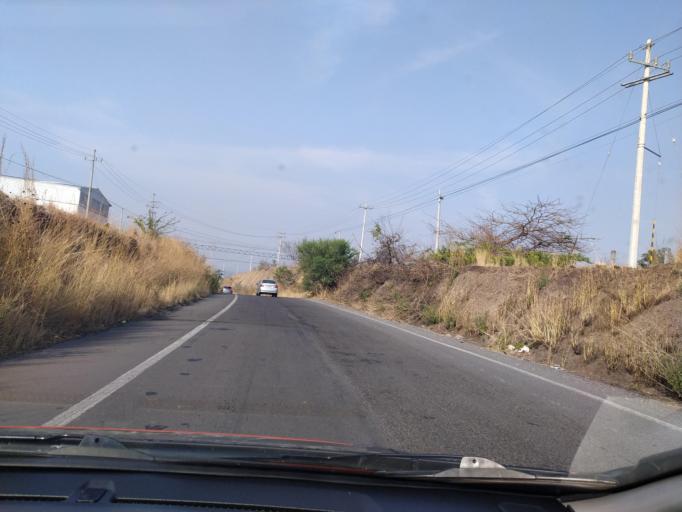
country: MX
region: Jalisco
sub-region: Acatlan de Juarez
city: Villa de los Ninos
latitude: 20.4331
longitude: -103.5805
